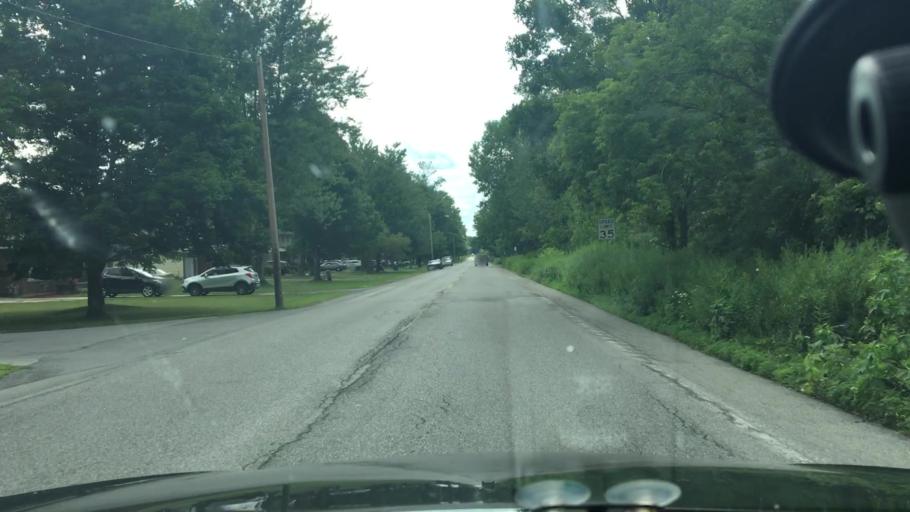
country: US
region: New York
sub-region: Erie County
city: Orchard Park
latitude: 42.7708
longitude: -78.7546
